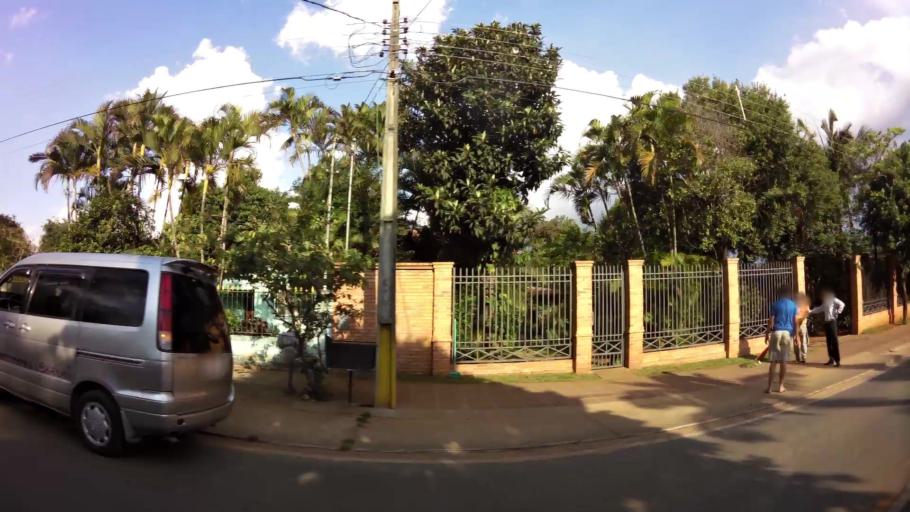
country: PY
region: Central
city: Fernando de la Mora
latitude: -25.3482
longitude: -57.5525
